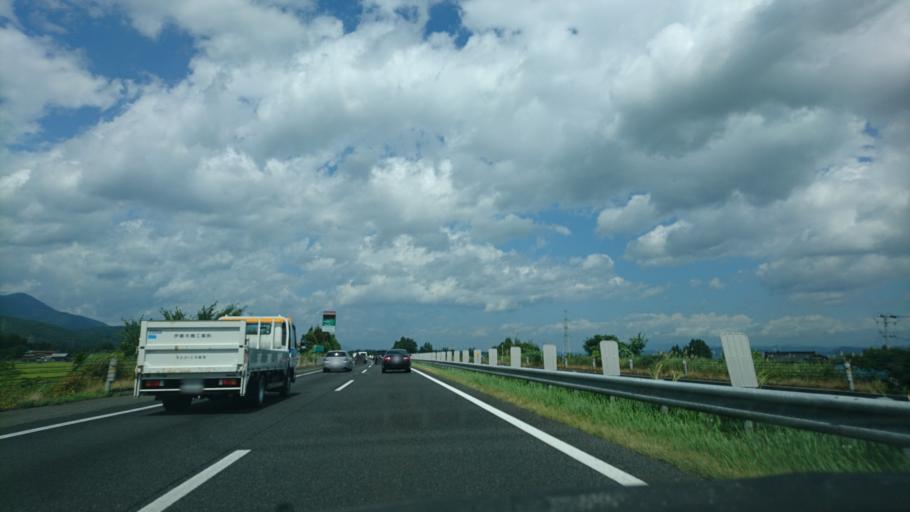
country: JP
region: Iwate
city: Morioka-shi
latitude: 39.5753
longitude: 141.1207
